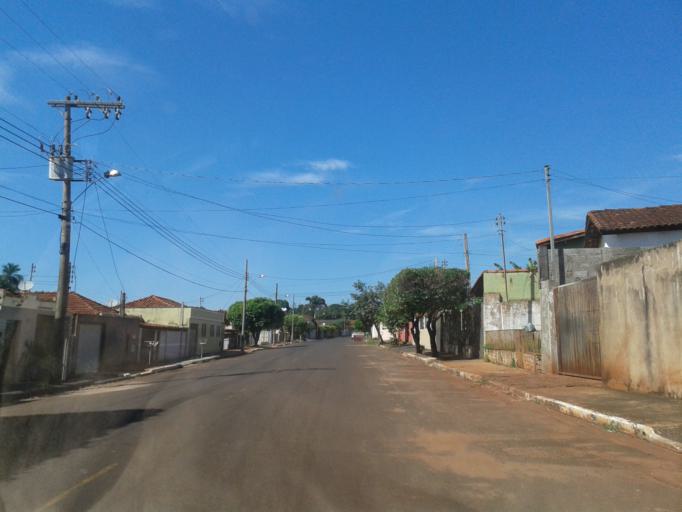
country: BR
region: Minas Gerais
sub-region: Ituiutaba
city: Ituiutaba
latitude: -18.9780
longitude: -49.4730
